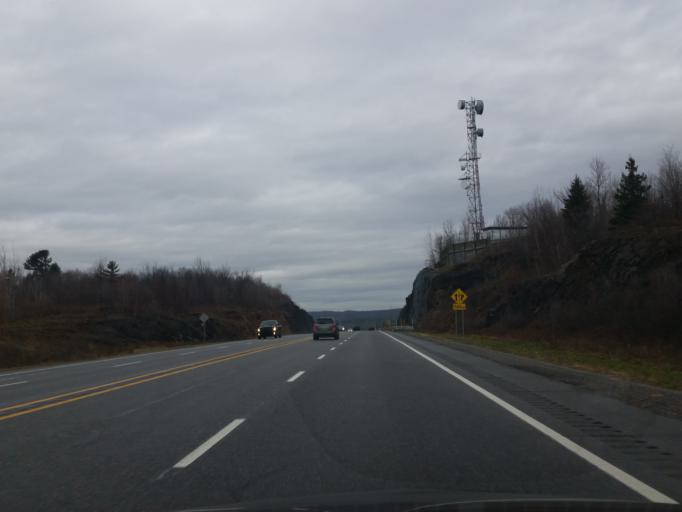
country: CA
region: Ontario
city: Clarence-Rockland
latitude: 45.5966
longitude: -75.3862
